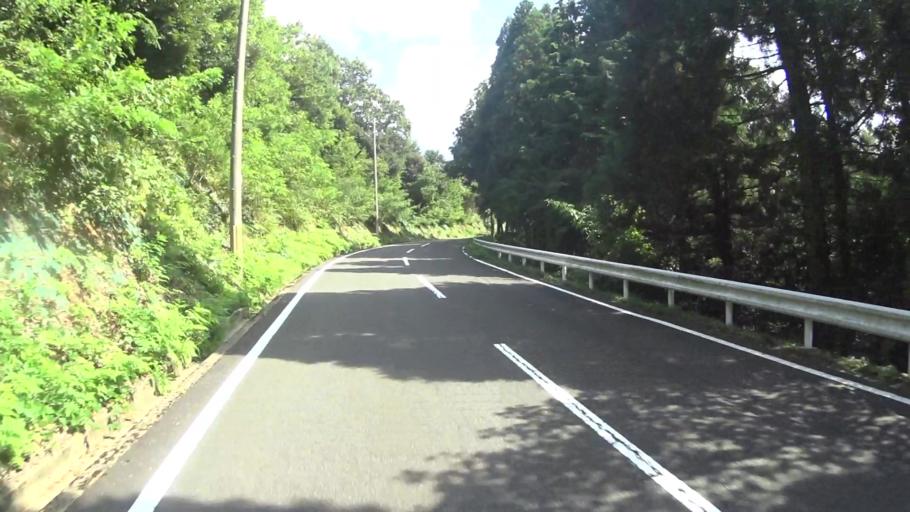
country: JP
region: Kyoto
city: Miyazu
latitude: 35.7495
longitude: 135.1683
